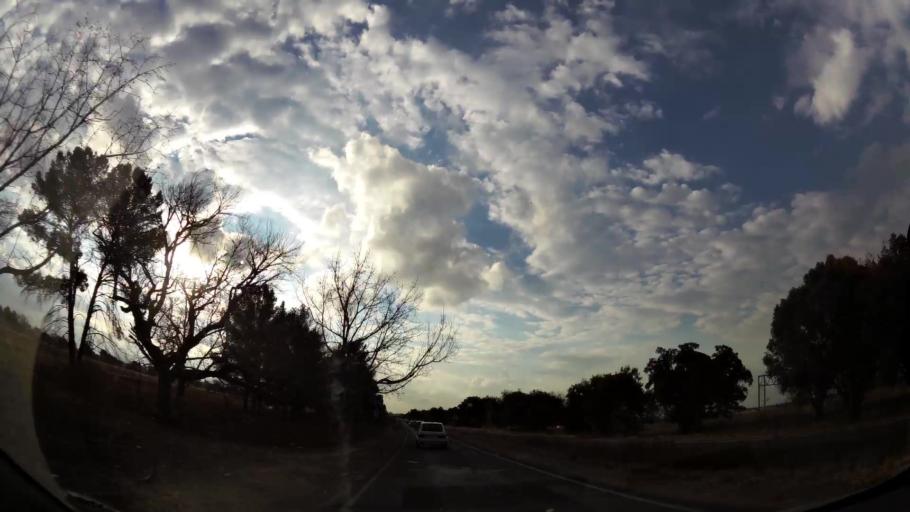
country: ZA
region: Orange Free State
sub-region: Fezile Dabi District Municipality
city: Sasolburg
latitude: -26.7996
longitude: 27.8315
